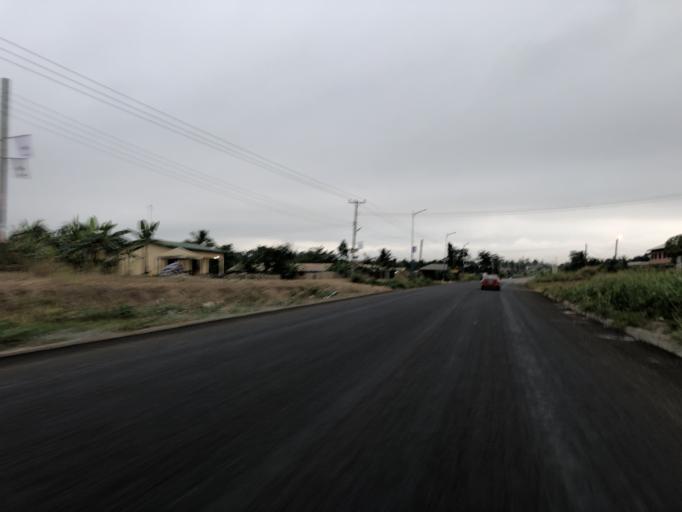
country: GH
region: Eastern
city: Koforidua
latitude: 6.1828
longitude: -0.3496
